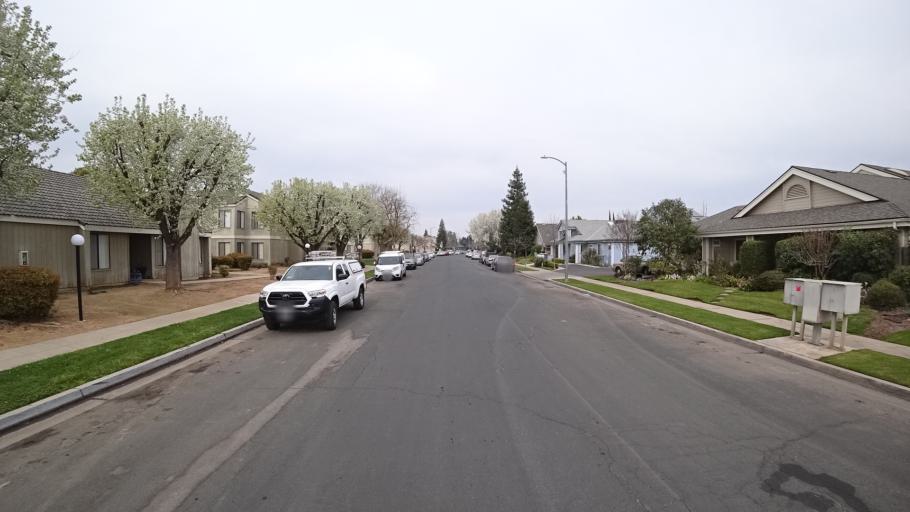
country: US
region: California
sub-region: Fresno County
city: Fresno
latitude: 36.8391
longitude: -119.8130
